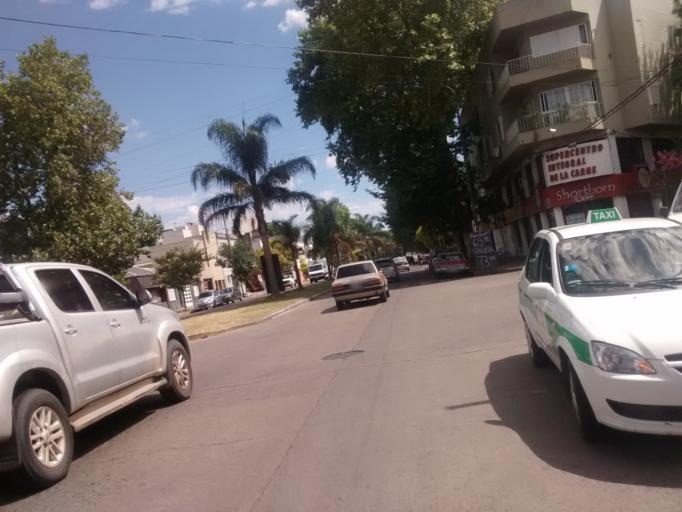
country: AR
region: Buenos Aires
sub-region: Partido de La Plata
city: La Plata
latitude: -34.9357
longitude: -57.9536
